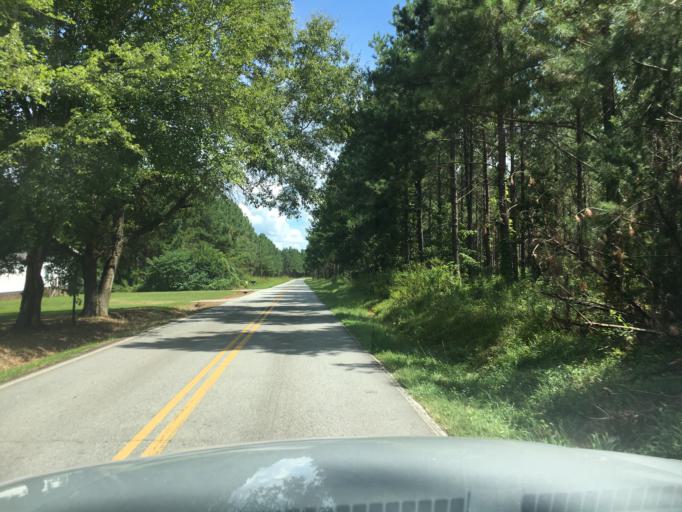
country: US
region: South Carolina
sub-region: Anderson County
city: Honea Path
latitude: 34.5003
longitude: -82.4072
